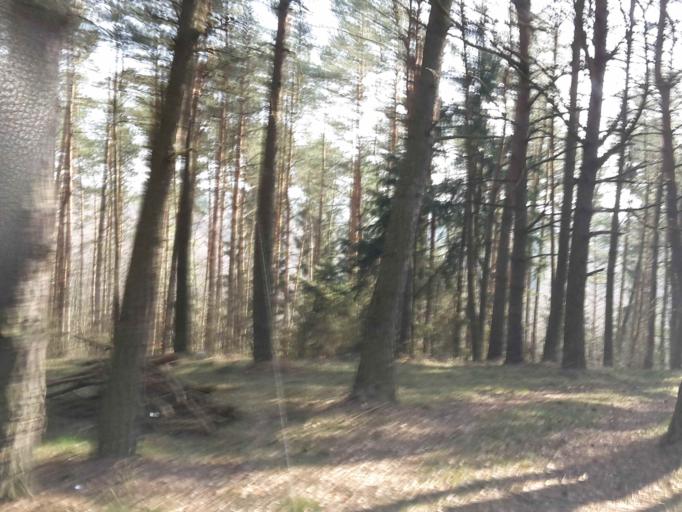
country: PL
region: Kujawsko-Pomorskie
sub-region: Powiat brodnicki
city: Brodnica
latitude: 53.3206
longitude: 19.3610
